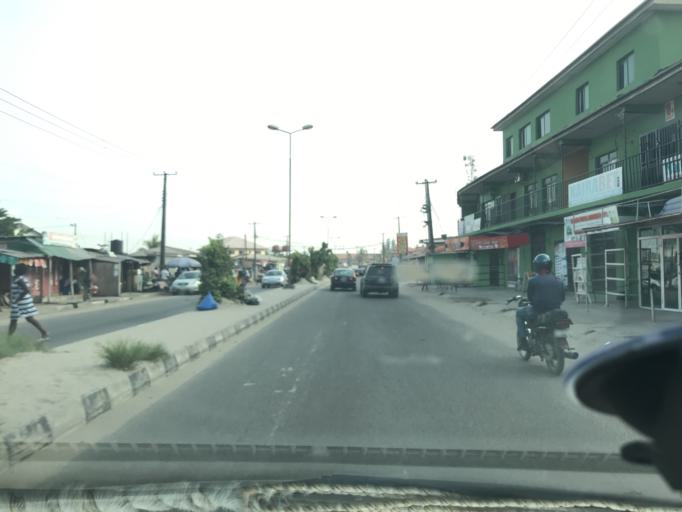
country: NG
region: Lagos
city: Ikorodu
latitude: 6.4960
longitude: 3.5838
